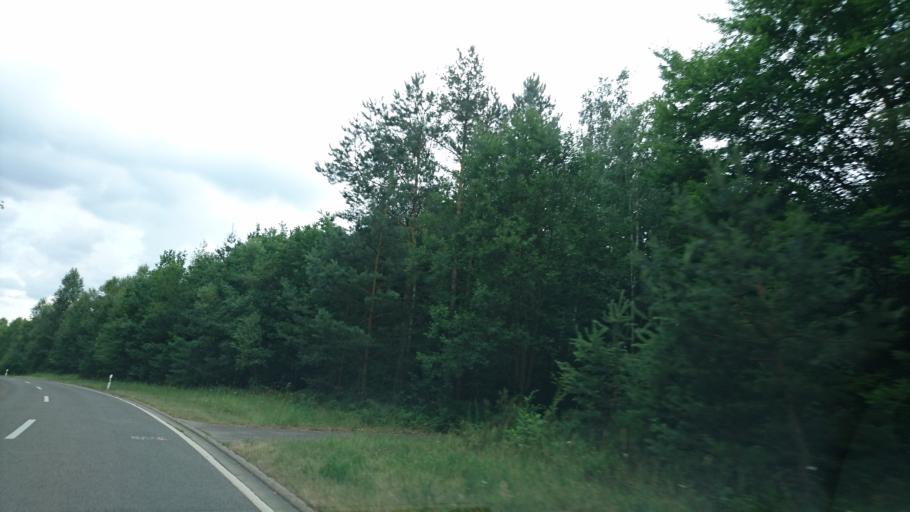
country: DE
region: Bavaria
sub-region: Regierungsbezirk Mittelfranken
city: Heideck
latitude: 49.1748
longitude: 11.1165
